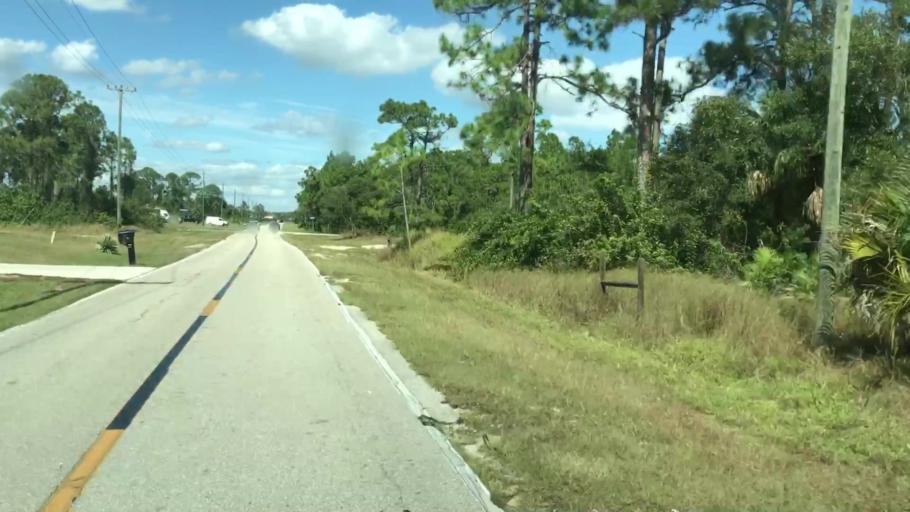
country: US
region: Florida
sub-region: Lee County
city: Lehigh Acres
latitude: 26.6648
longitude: -81.6257
